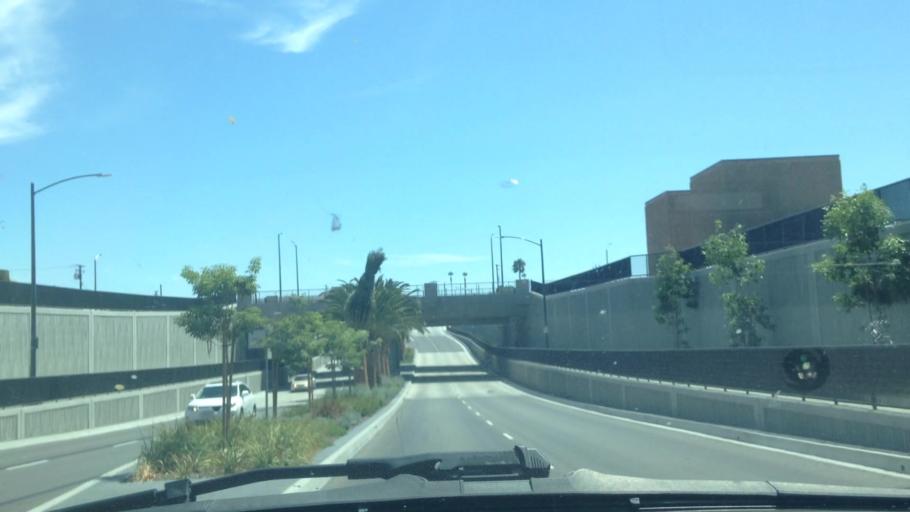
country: US
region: California
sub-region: Orange County
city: Fullerton
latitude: 33.8678
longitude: -117.9070
